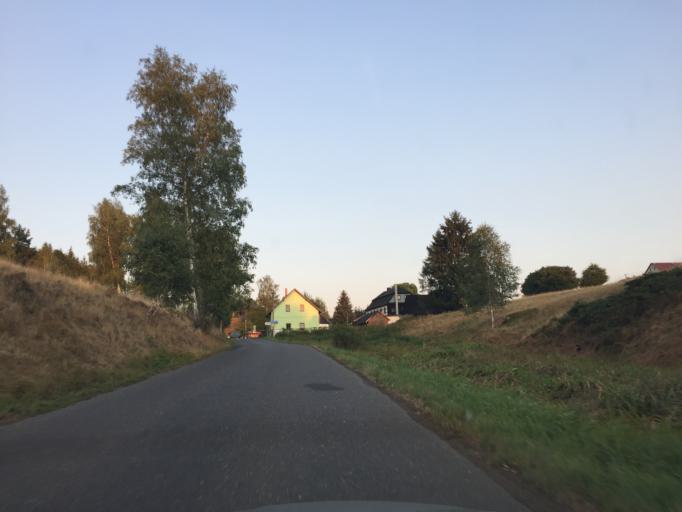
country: CZ
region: Ustecky
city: Ceska Kamenice
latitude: 50.8626
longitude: 14.3528
